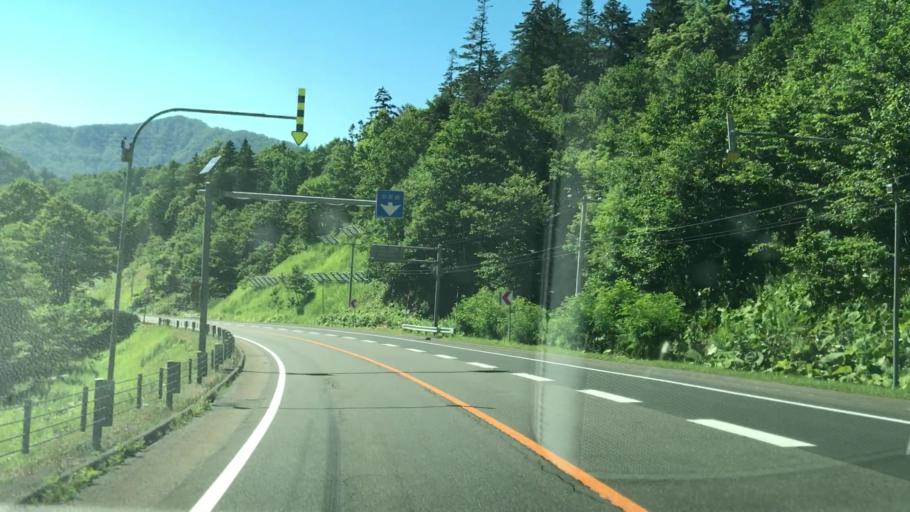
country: JP
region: Hokkaido
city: Shimo-furano
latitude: 42.9636
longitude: 142.6525
